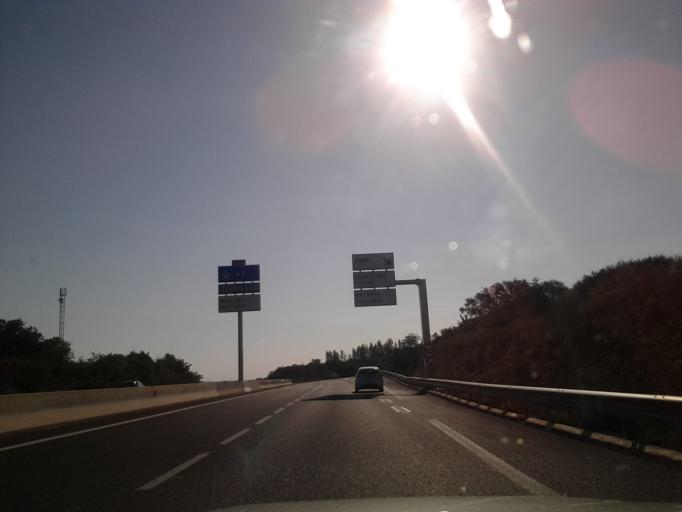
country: FR
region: Languedoc-Roussillon
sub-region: Departement des Pyrenees-Orientales
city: Ille-sur-Tet
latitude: 42.6601
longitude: 2.5973
